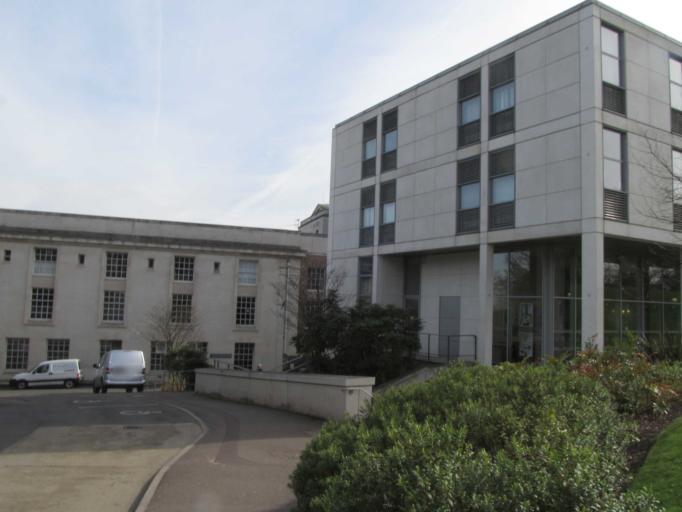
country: GB
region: England
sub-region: Nottingham
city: Nottingham
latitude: 52.9388
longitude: -1.1942
